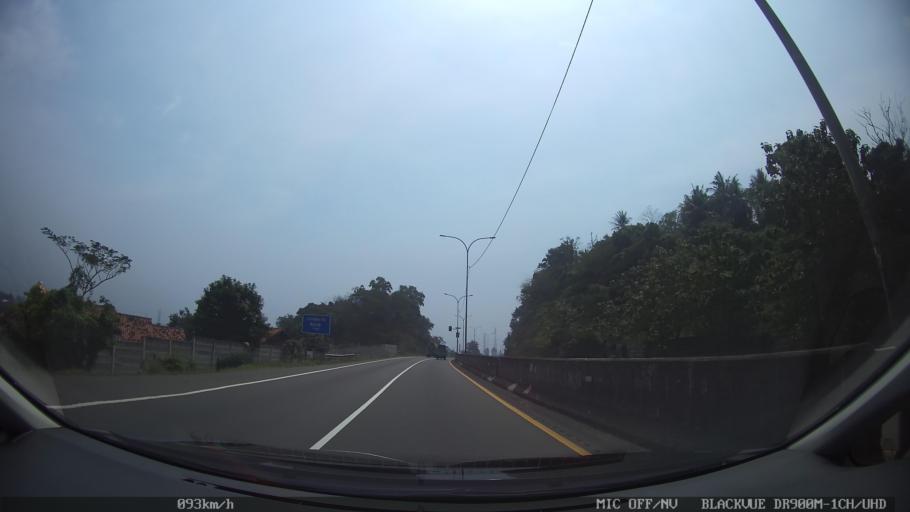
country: ID
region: Banten
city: Curug
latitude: -5.9784
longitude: 106.0161
